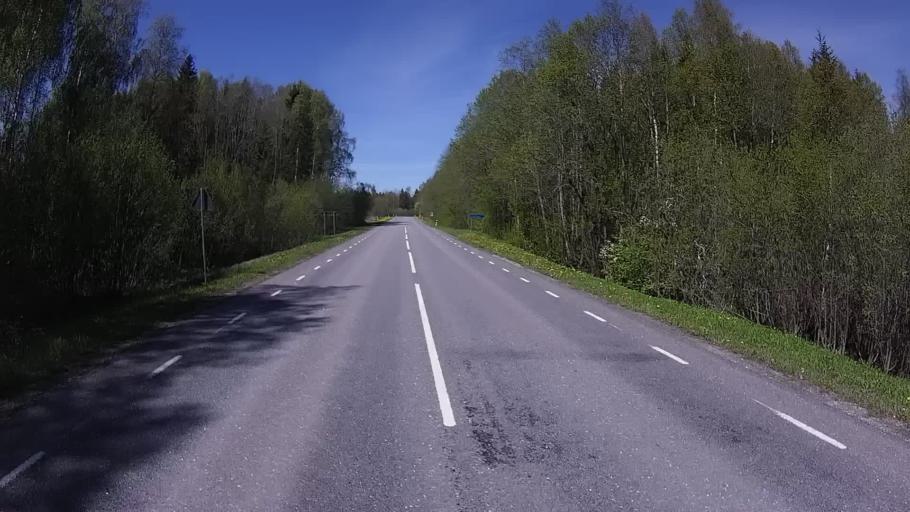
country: EE
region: Raplamaa
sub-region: Kehtna vald
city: Kehtna
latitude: 59.0437
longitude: 25.0292
